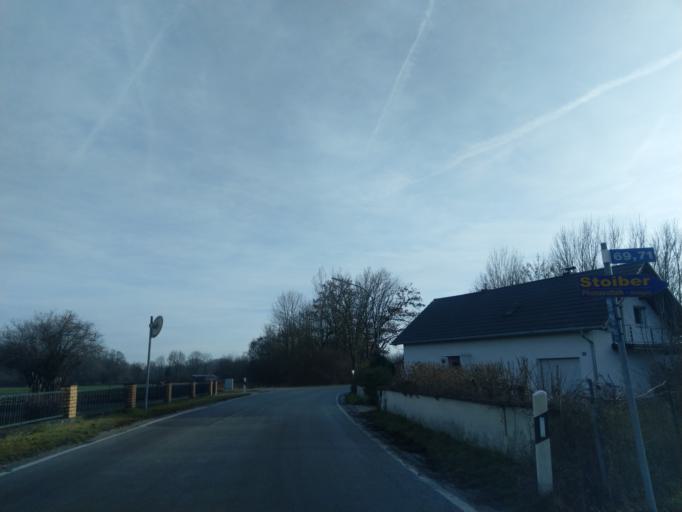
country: DE
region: Bavaria
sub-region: Lower Bavaria
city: Oberporing
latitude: 48.7130
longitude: 12.8116
